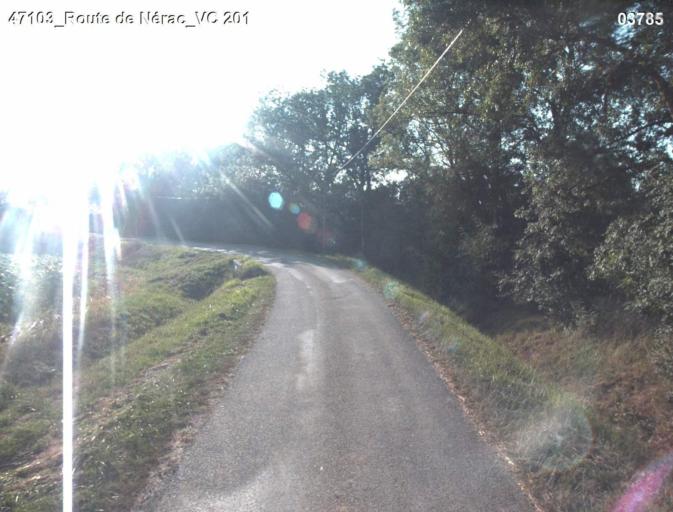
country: FR
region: Aquitaine
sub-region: Departement du Lot-et-Garonne
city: Mezin
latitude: 44.0823
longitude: 0.3110
